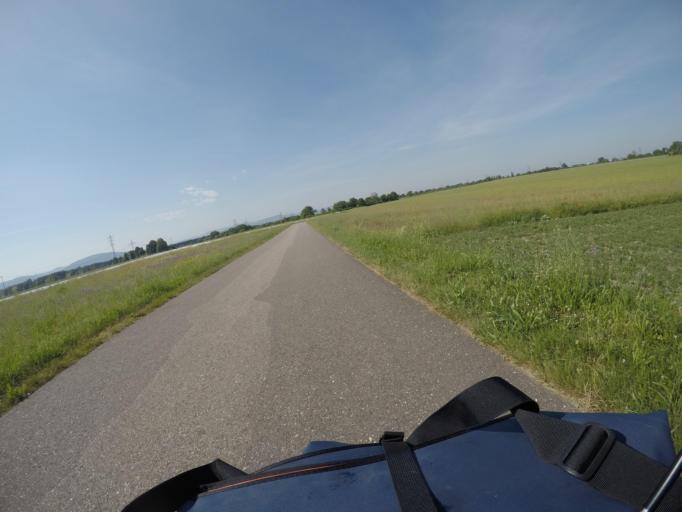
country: DE
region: Baden-Wuerttemberg
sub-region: Karlsruhe Region
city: Durmersheim
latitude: 48.9133
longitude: 8.2772
